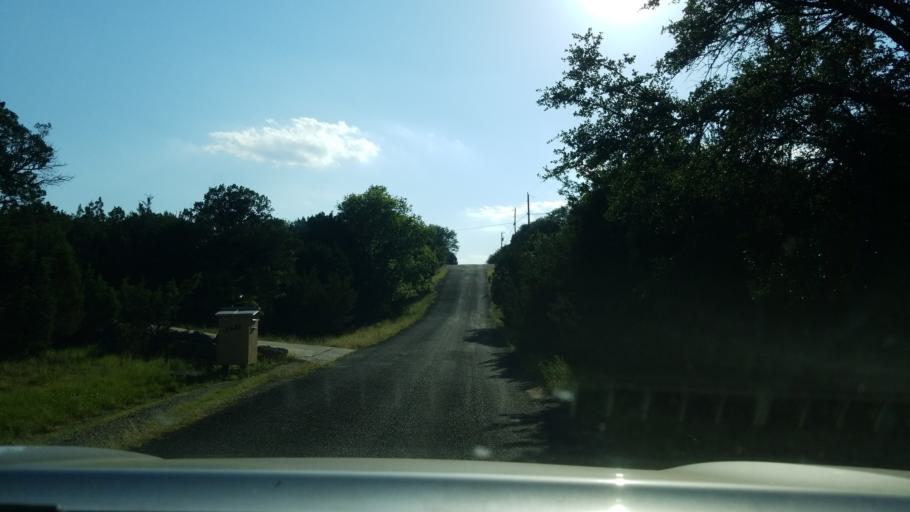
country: US
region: Texas
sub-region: Comal County
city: Bulverde
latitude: 29.7828
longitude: -98.4485
